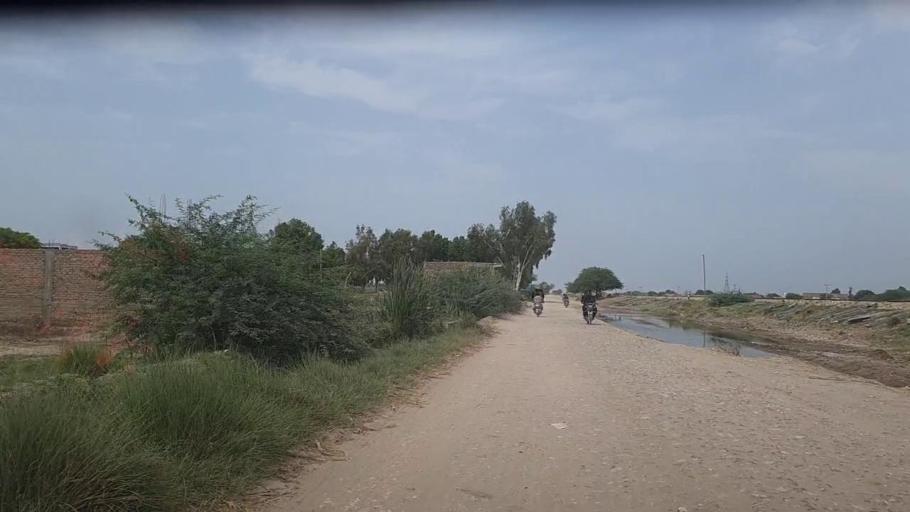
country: PK
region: Sindh
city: Bhiria
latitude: 26.8979
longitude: 68.2874
